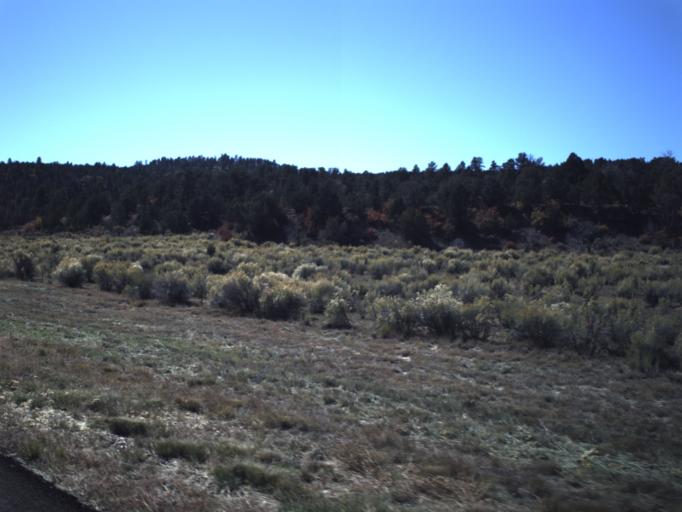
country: US
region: Utah
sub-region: Garfield County
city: Panguitch
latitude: 37.6686
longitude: -111.8303
